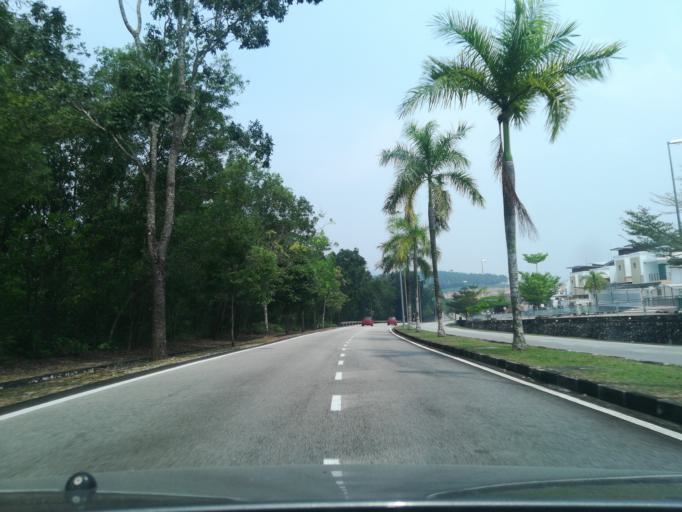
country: MY
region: Kedah
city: Kulim
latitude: 5.3972
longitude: 100.5801
